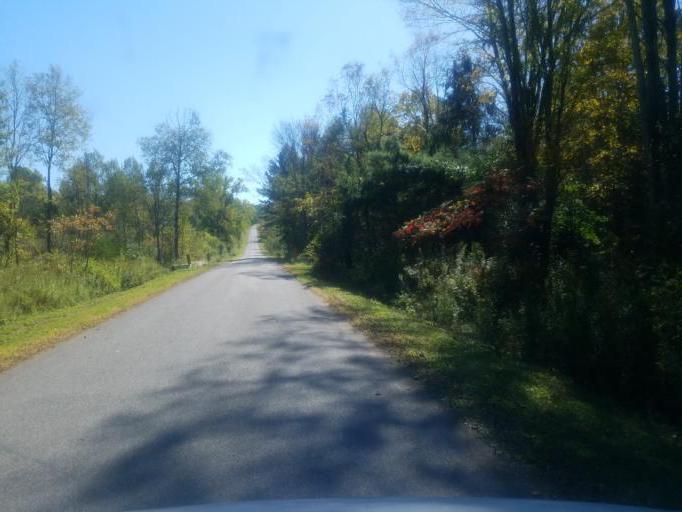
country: US
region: New York
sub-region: Allegany County
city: Houghton
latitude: 42.3218
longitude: -78.2068
